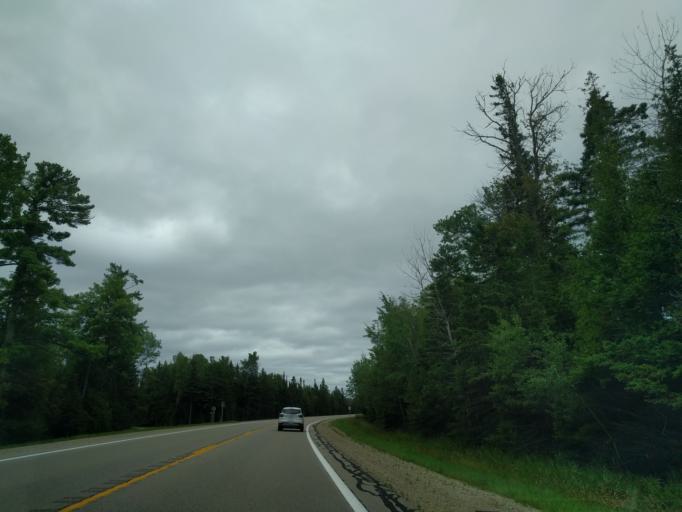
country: US
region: Michigan
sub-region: Delta County
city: Escanaba
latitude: 45.4469
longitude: -87.3386
